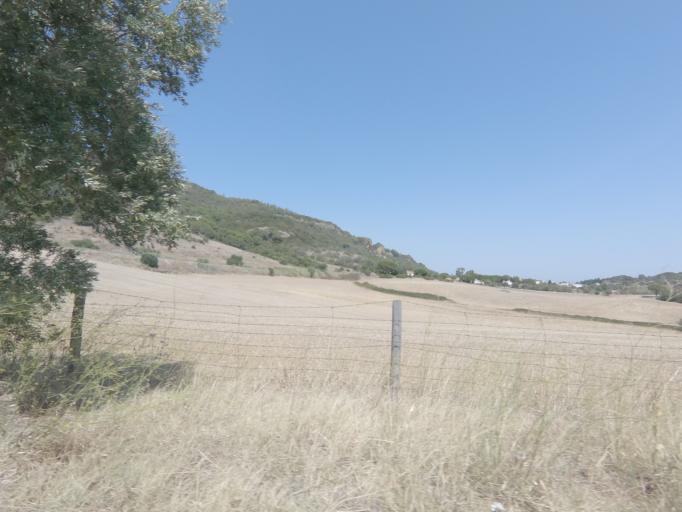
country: PT
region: Setubal
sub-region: Palmela
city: Quinta do Anjo
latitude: 38.5250
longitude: -8.9332
